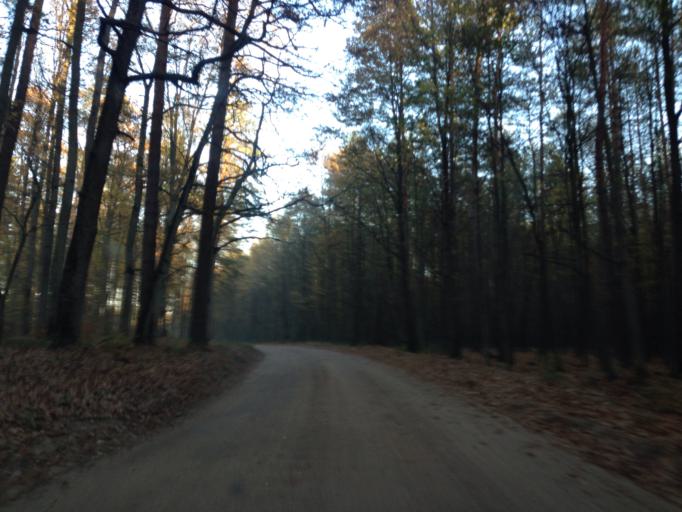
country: PL
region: Kujawsko-Pomorskie
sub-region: Powiat brodnicki
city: Gorzno
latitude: 53.2004
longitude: 19.7017
